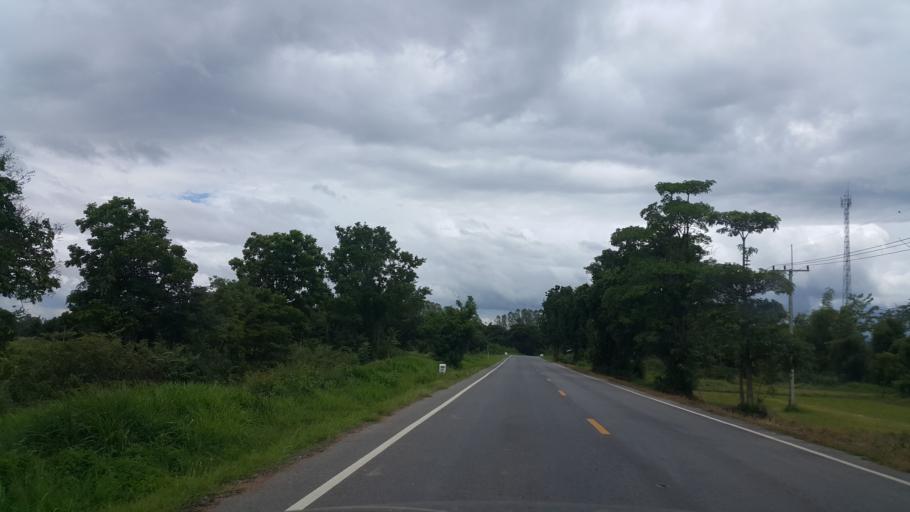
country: TH
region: Sukhothai
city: Ban Na
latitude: 17.0477
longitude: 99.7041
